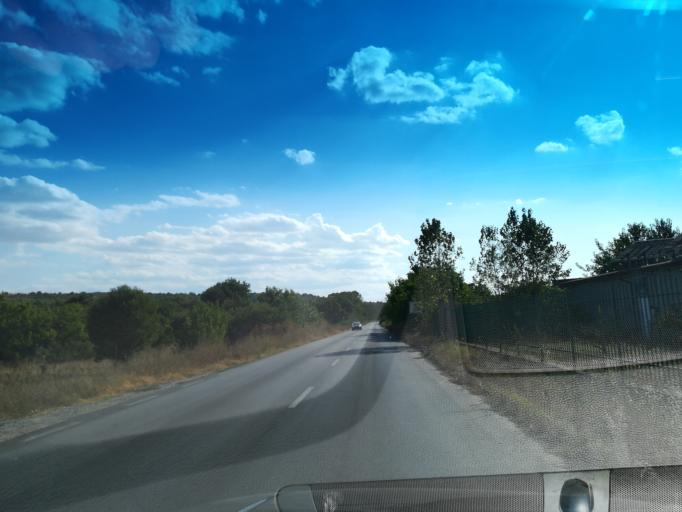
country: BG
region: Khaskovo
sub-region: Obshtina Mineralni Bani
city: Mineralni Bani
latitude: 42.0192
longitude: 25.4107
